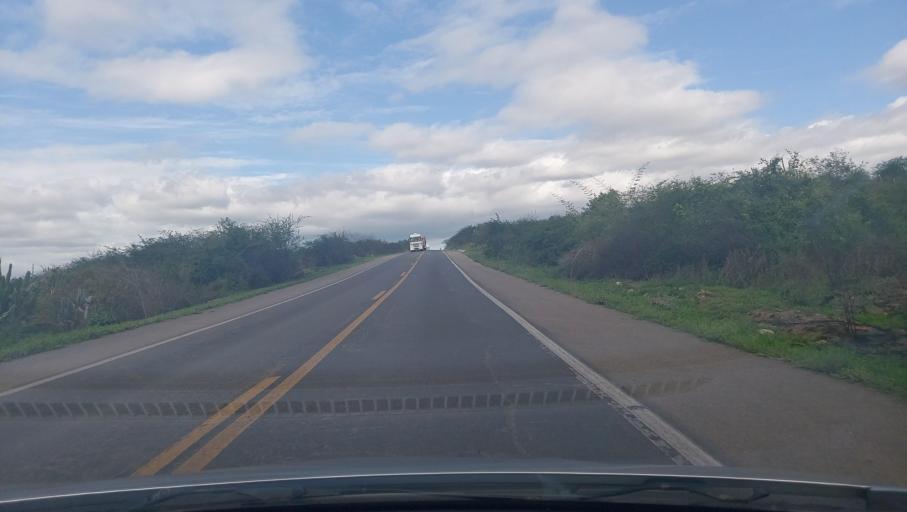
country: BR
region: Bahia
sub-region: Ipira
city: Ipira
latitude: -12.4984
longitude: -39.6712
